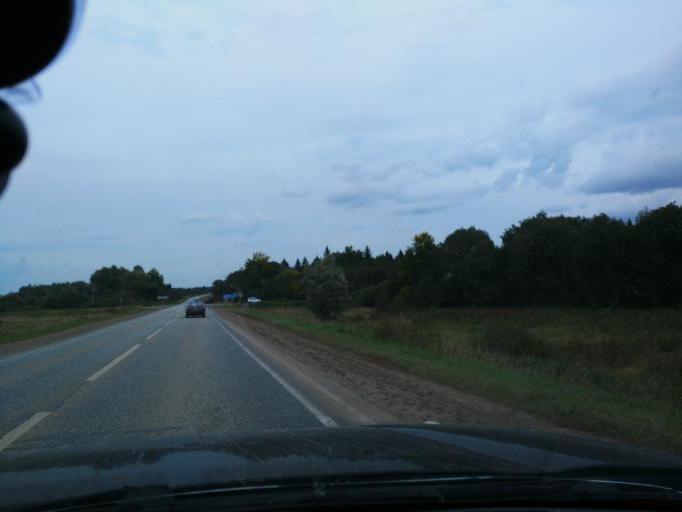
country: RU
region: Perm
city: Chernushka
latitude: 56.5186
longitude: 56.0159
